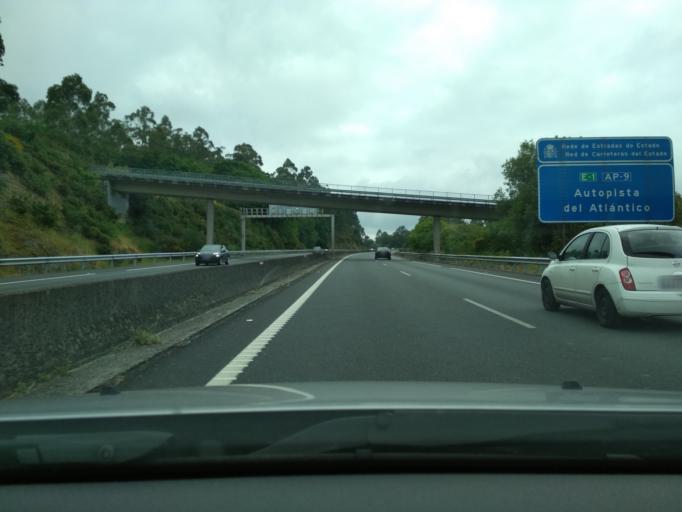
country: ES
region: Galicia
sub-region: Provincia da Coruna
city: Santiago de Compostela
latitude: 42.8495
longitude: -8.5714
